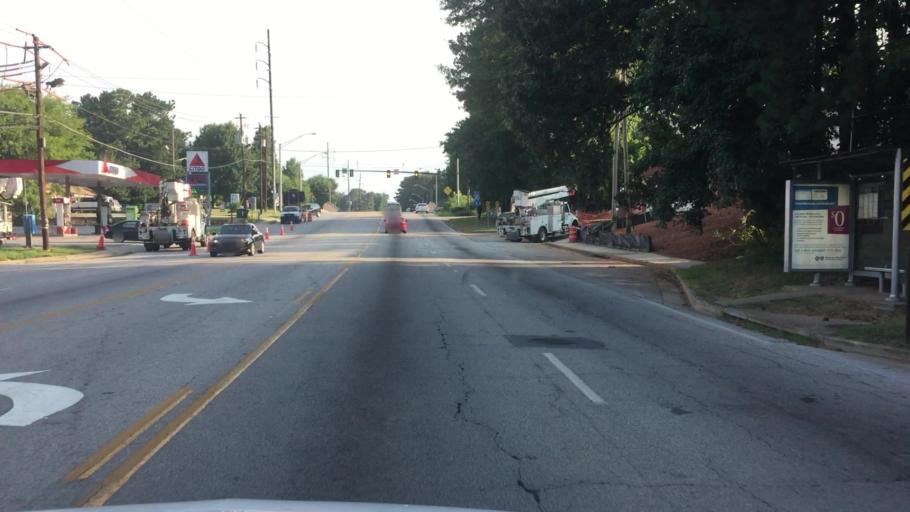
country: US
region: Georgia
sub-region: DeKalb County
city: Panthersville
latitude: 33.7141
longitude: -84.2524
